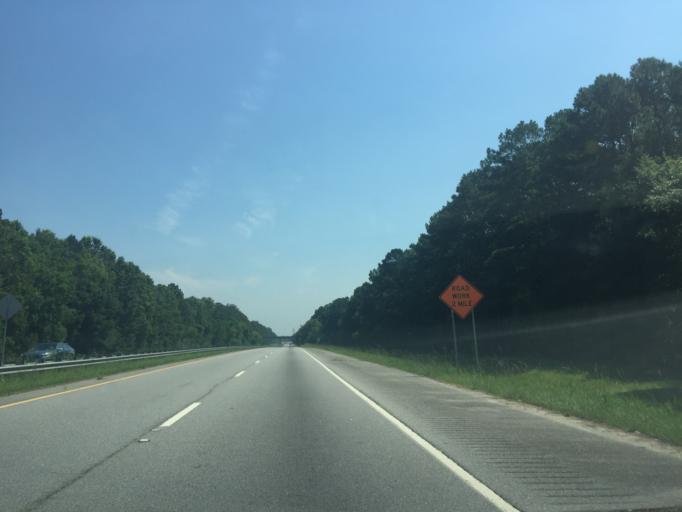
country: US
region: Georgia
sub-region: Chatham County
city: Georgetown
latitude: 32.0231
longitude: -81.1717
